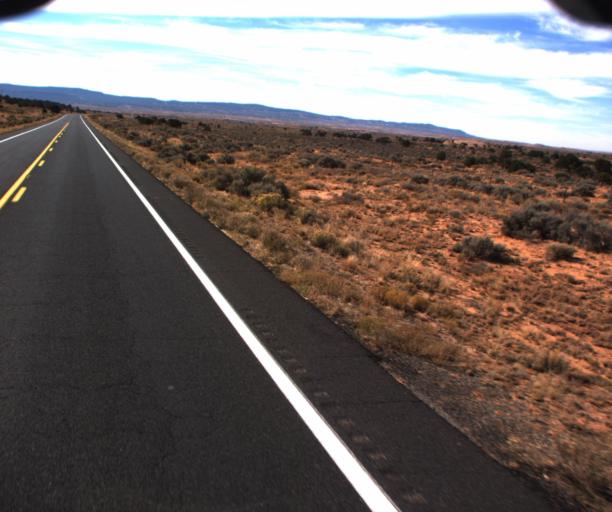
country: US
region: Arizona
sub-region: Coconino County
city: Kaibito
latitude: 36.5323
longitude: -110.7013
